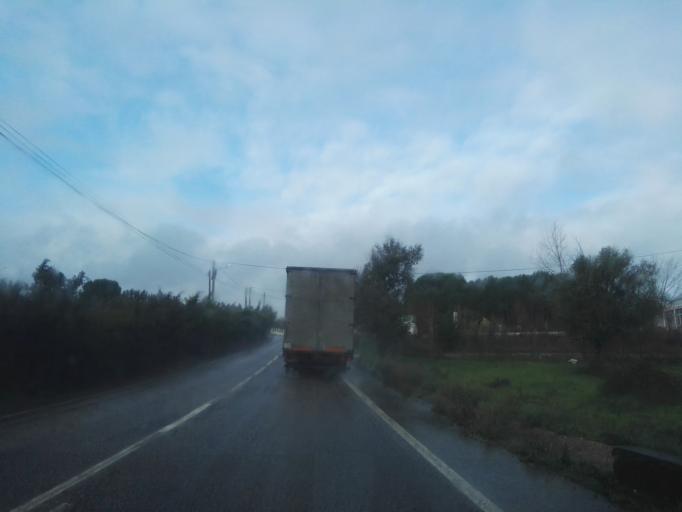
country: PT
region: Santarem
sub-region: Cartaxo
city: Cartaxo
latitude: 39.1910
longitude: -8.7978
